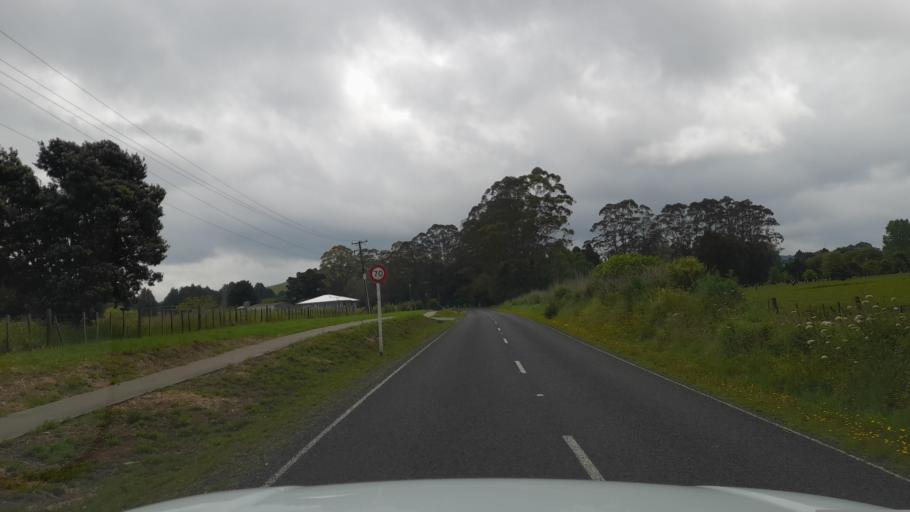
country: NZ
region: Northland
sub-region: Far North District
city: Waimate North
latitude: -35.4183
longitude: 173.7925
